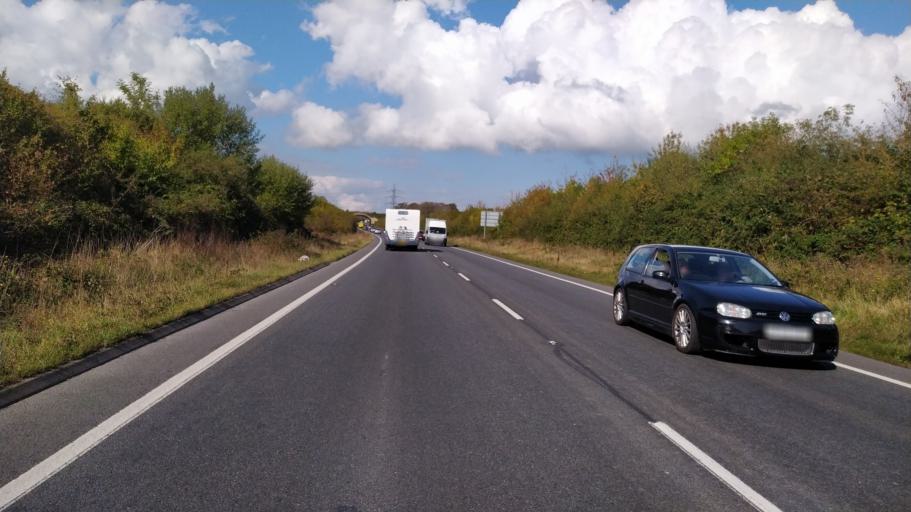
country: GB
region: England
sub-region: Dorset
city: Weymouth
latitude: 50.6396
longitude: -2.4634
